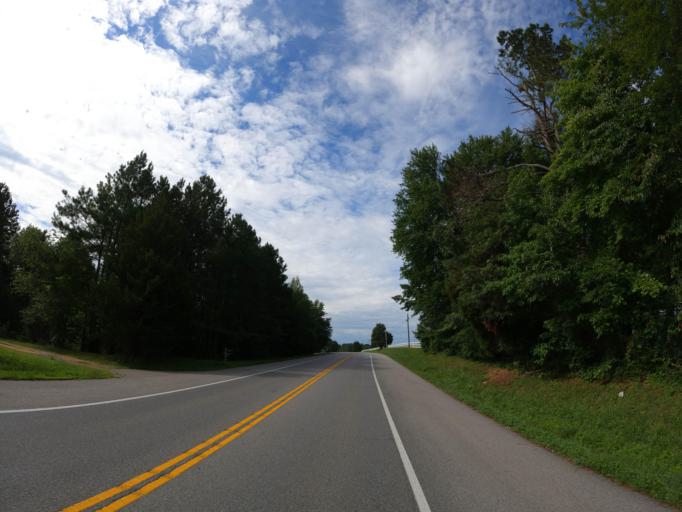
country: US
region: Maryland
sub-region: Saint Mary's County
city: Mechanicsville
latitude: 38.4126
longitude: -76.7184
